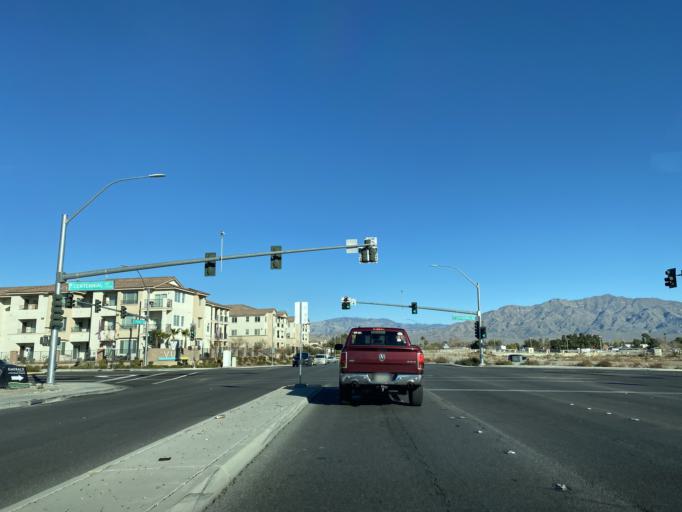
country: US
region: Nevada
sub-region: Clark County
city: Las Vegas
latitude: 36.2764
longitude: -115.2516
